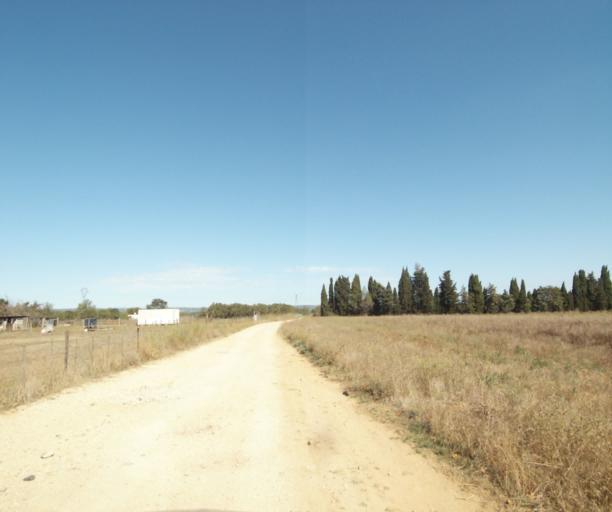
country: FR
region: Languedoc-Roussillon
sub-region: Departement du Gard
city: Bouillargues
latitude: 43.8055
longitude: 4.4489
